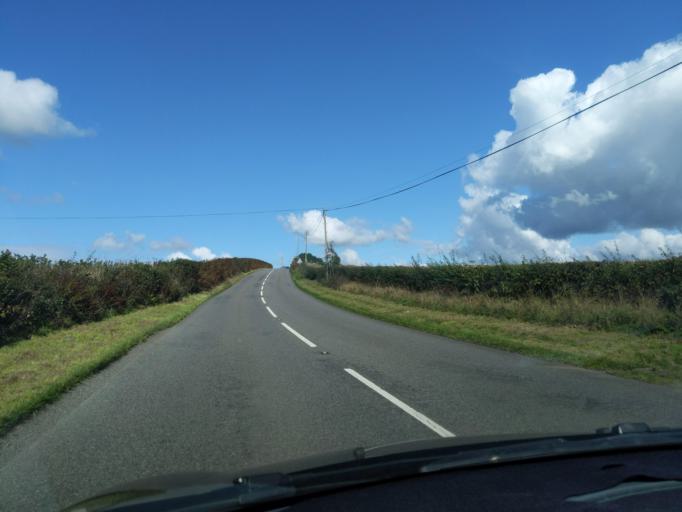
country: GB
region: England
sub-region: Cornwall
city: Boyton
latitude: 50.7182
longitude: -4.3290
